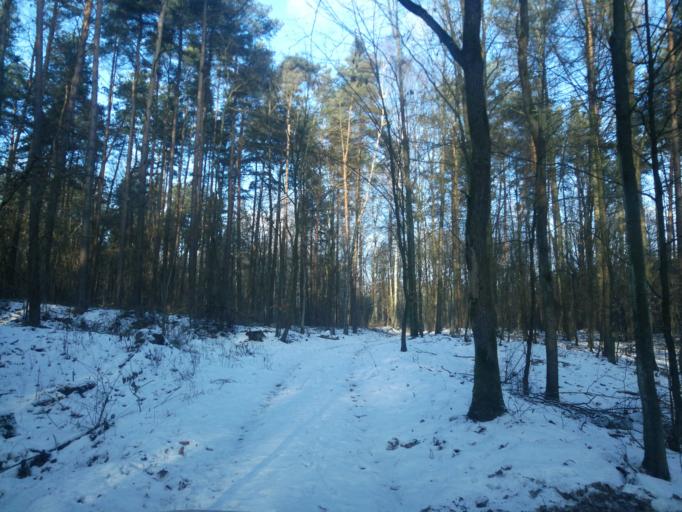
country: PL
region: Kujawsko-Pomorskie
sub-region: Powiat brodnicki
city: Gorzno
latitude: 53.2177
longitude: 19.6480
